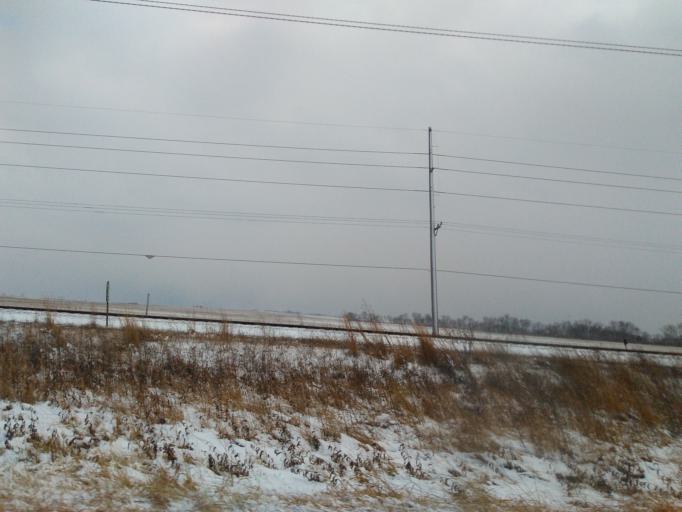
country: US
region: Illinois
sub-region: Madison County
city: Saint Jacob
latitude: 38.7297
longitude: -89.7291
